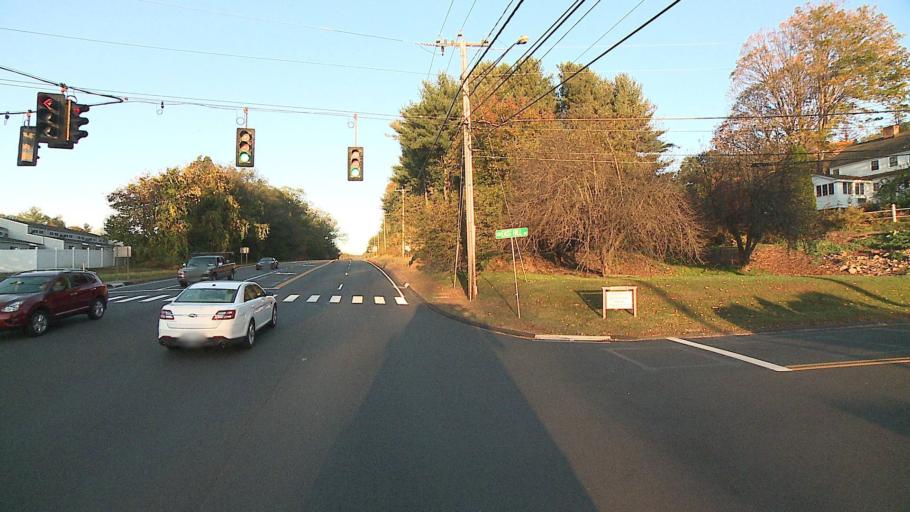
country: US
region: Connecticut
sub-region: Hartford County
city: Canton Valley
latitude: 41.8313
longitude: -72.9086
